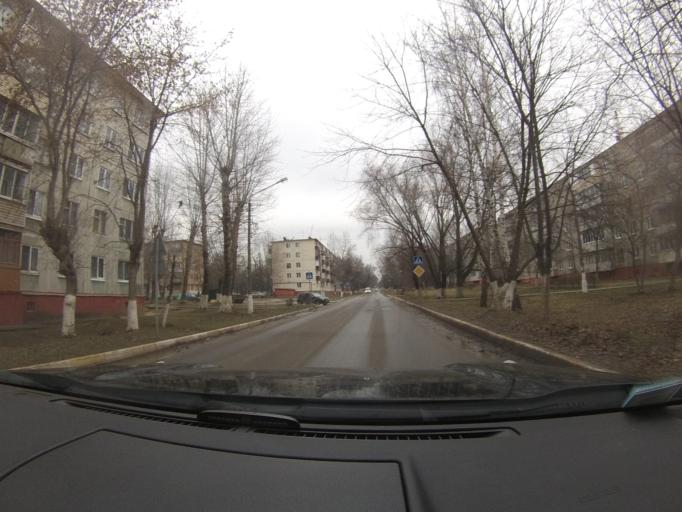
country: RU
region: Moskovskaya
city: Peski
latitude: 55.2724
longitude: 38.7479
